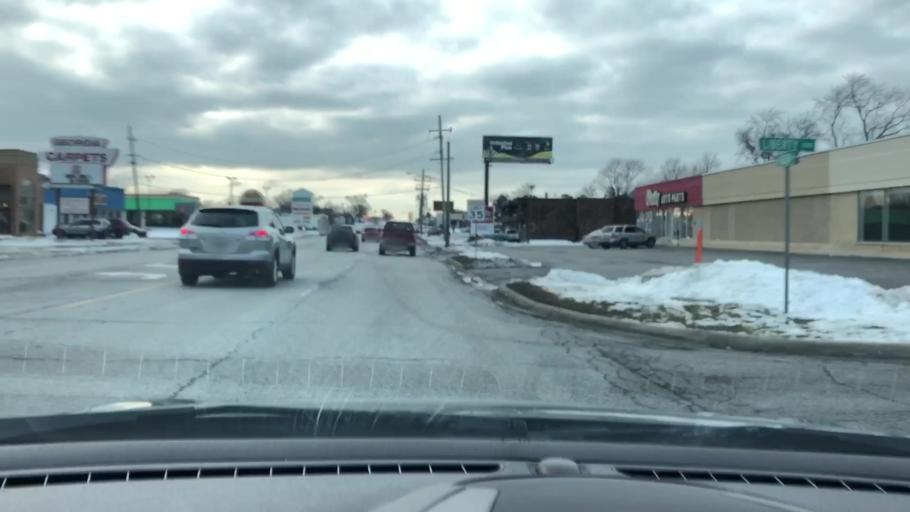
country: US
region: Illinois
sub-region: DuPage County
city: Westmont
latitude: 41.8099
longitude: -87.9830
